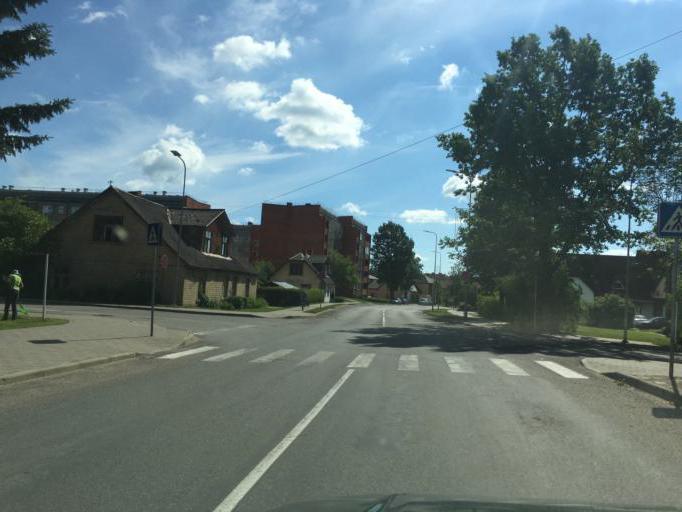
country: LV
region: Balvu Rajons
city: Balvi
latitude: 57.1320
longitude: 27.2704
